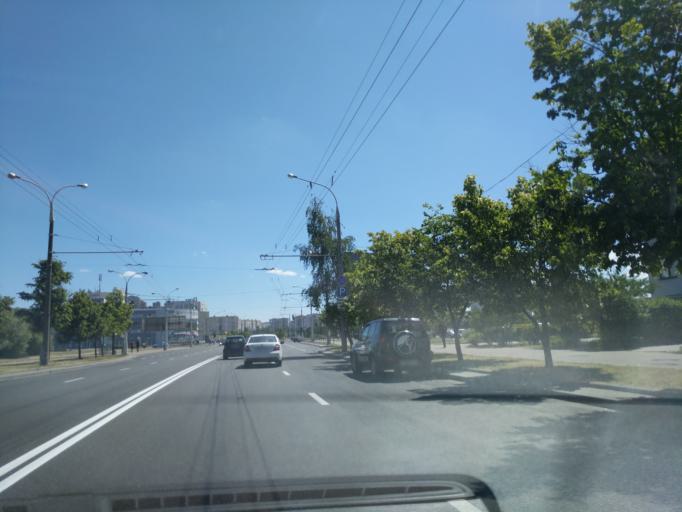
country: BY
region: Minsk
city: Borovlyany
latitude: 53.9487
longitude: 27.6793
